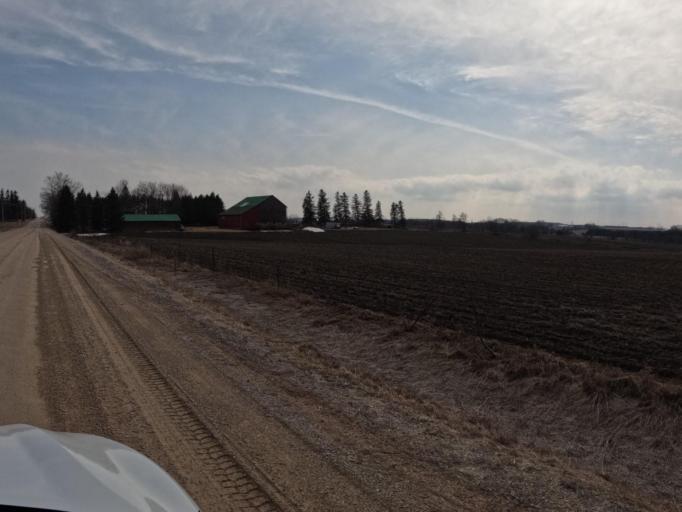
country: CA
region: Ontario
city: Orangeville
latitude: 43.8881
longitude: -80.2986
